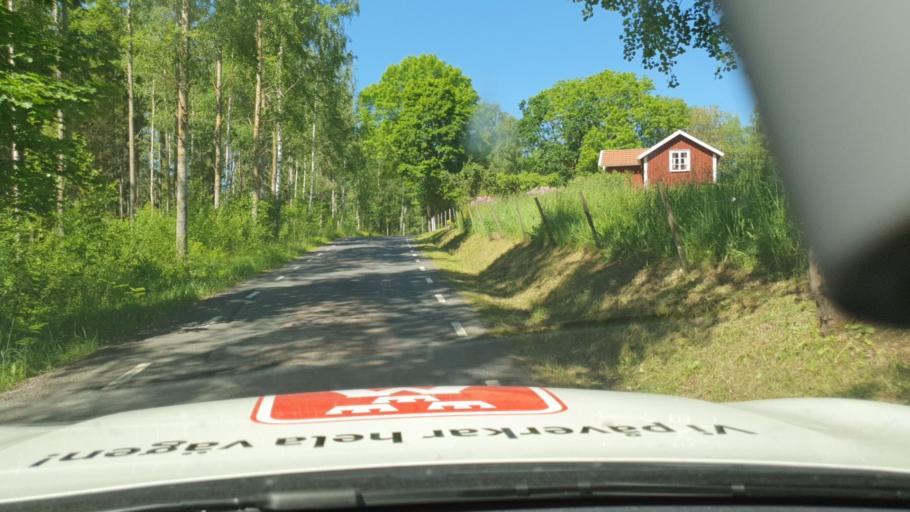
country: SE
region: Joenkoeping
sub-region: Habo Kommun
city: Habo
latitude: 57.9052
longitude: 14.0496
